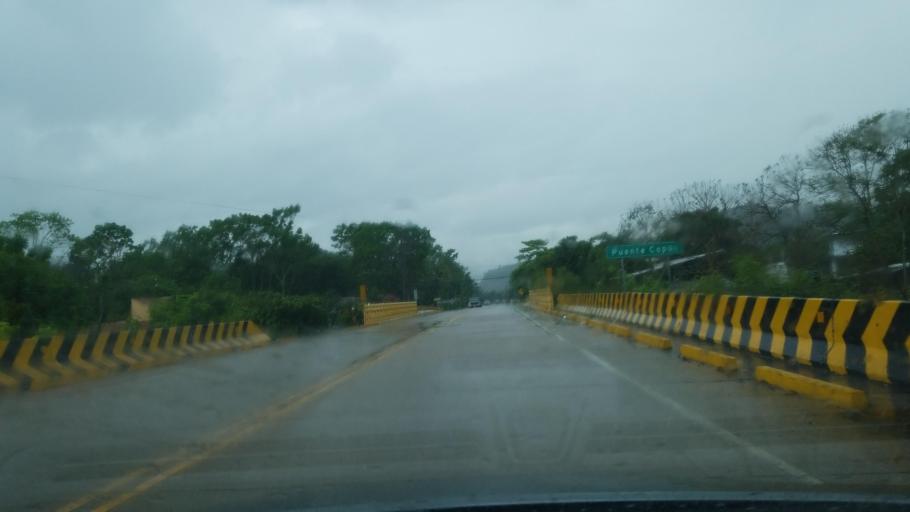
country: HN
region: Copan
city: Copan
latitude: 14.8353
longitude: -89.1526
